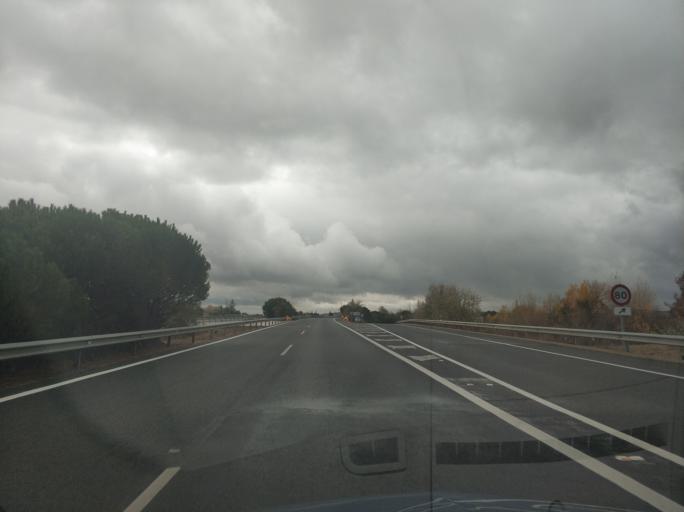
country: ES
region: Castille and Leon
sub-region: Provincia de Palencia
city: Soto de Cerrato
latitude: 41.9831
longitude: -4.4331
